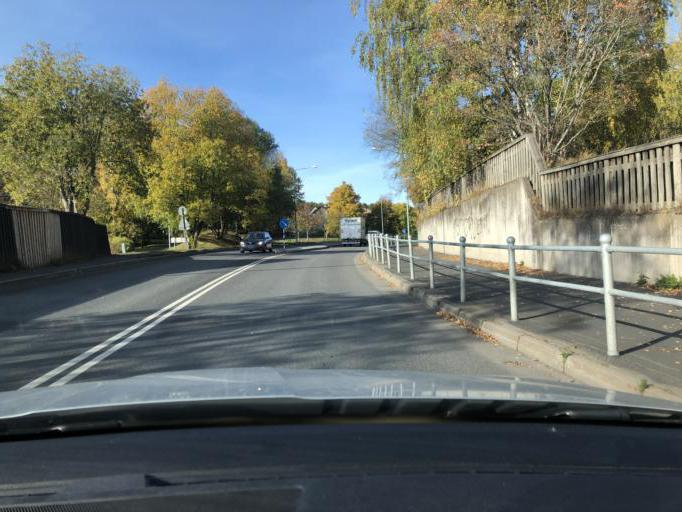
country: SE
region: Joenkoeping
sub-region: Jonkopings Kommun
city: Jonkoping
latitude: 57.7721
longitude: 14.1322
